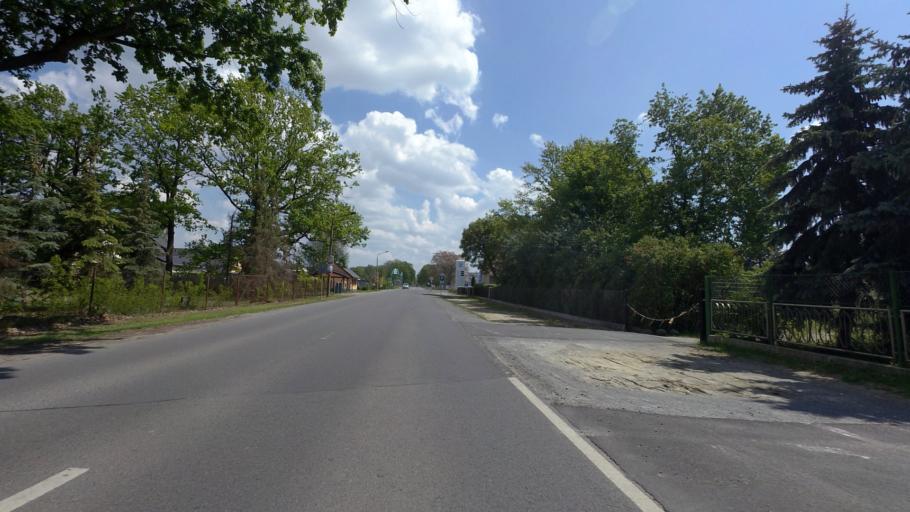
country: DE
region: Brandenburg
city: Luebben
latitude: 51.9415
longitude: 13.9221
